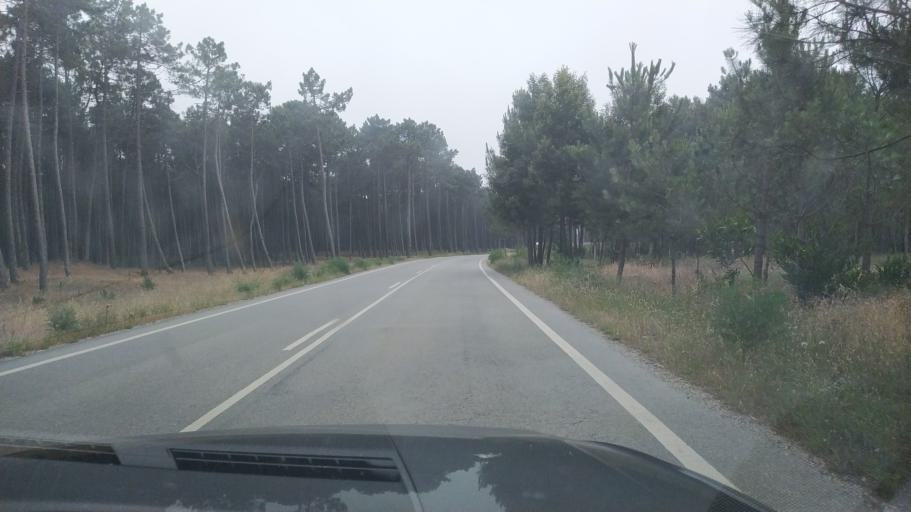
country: PT
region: Aveiro
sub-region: Ilhavo
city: Gafanha da Encarnacao
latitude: 40.5967
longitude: -8.7242
